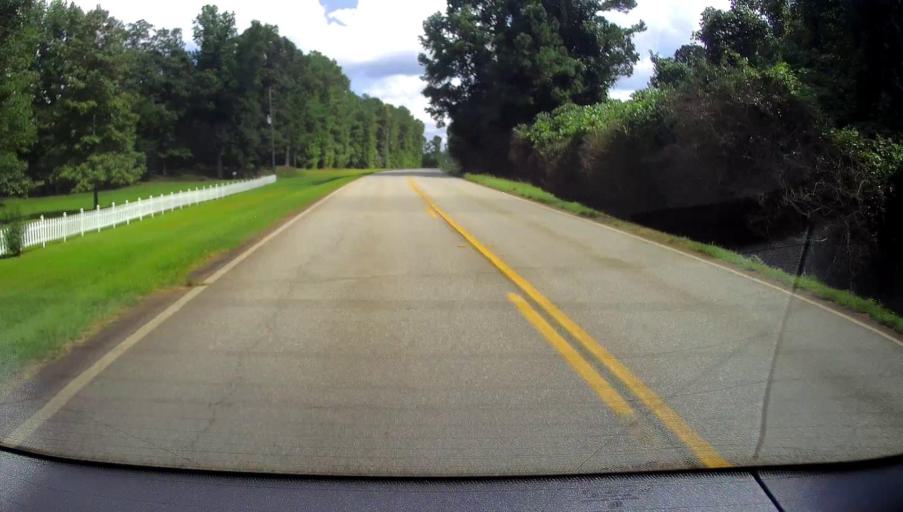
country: US
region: Georgia
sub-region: Crawford County
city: Knoxville
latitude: 32.8803
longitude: -83.9984
